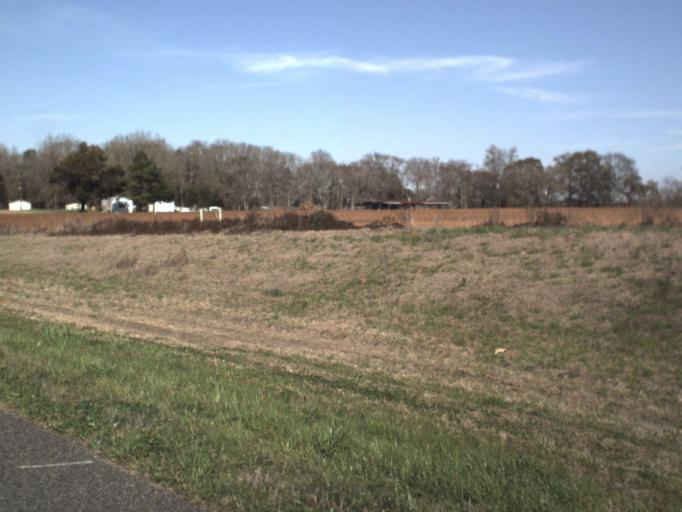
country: US
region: Florida
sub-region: Jackson County
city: Graceville
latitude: 30.9165
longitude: -85.3808
